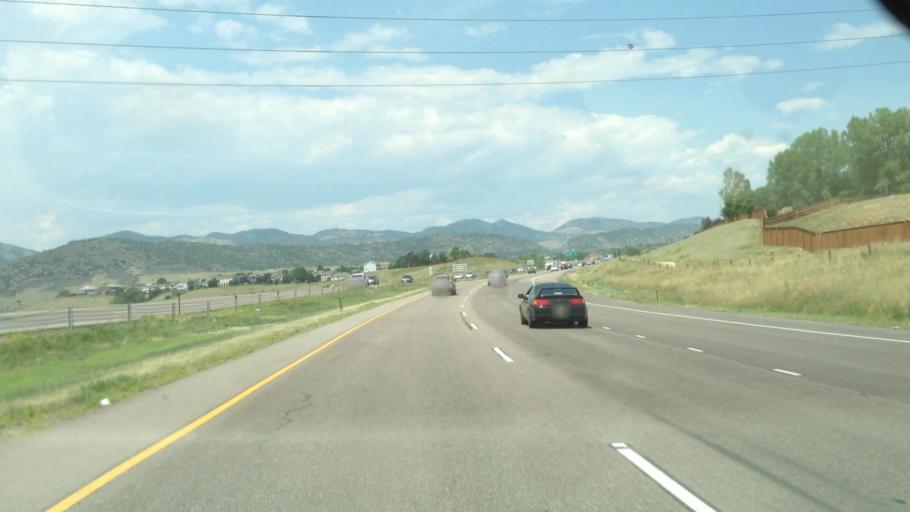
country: US
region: Colorado
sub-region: Jefferson County
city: Ken Caryl
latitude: 39.5541
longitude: -105.0920
